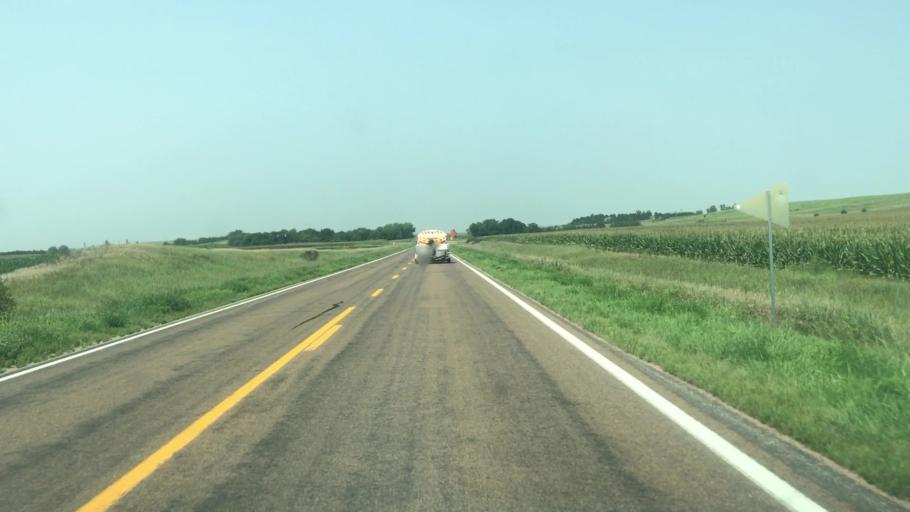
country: US
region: Nebraska
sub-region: Sherman County
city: Loup City
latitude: 41.2534
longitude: -98.9390
